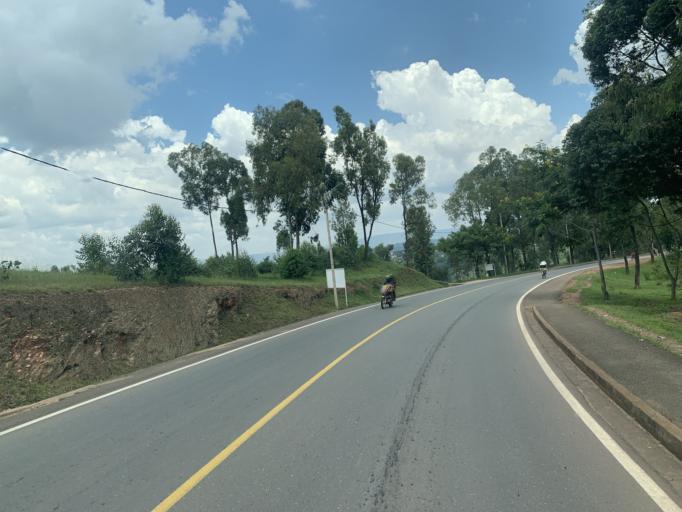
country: RW
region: Kigali
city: Kigali
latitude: -1.9994
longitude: 29.9054
